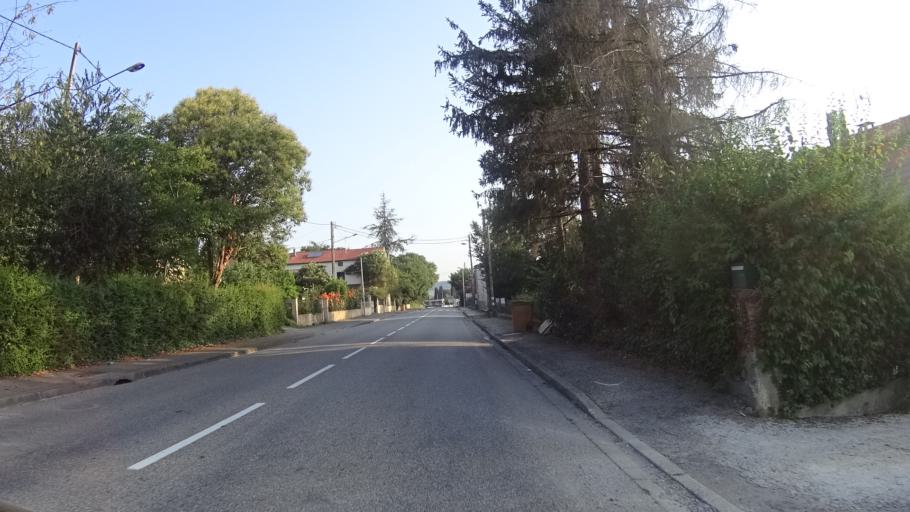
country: FR
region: Midi-Pyrenees
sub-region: Departement de l'Ariege
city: Mirepoix
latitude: 43.0820
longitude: 1.8766
